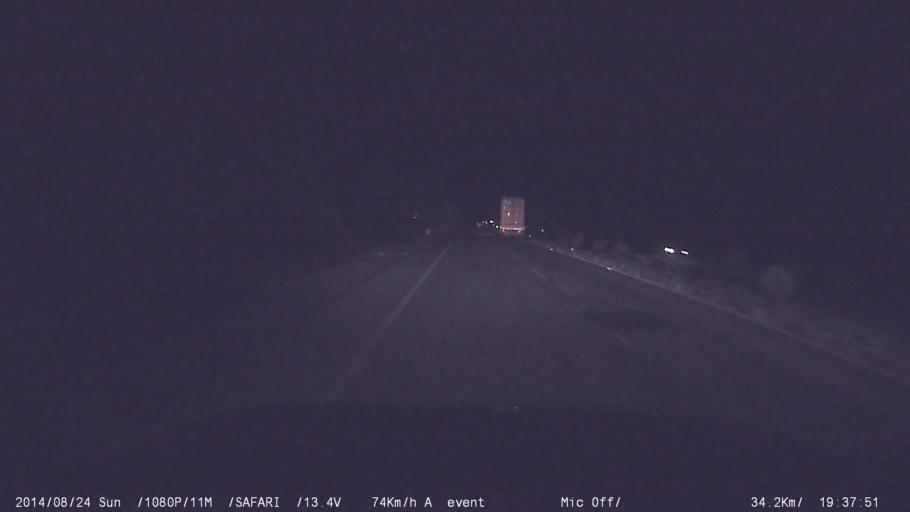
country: IN
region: Tamil Nadu
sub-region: Vellore
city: Walajapet
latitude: 12.9027
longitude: 79.4265
